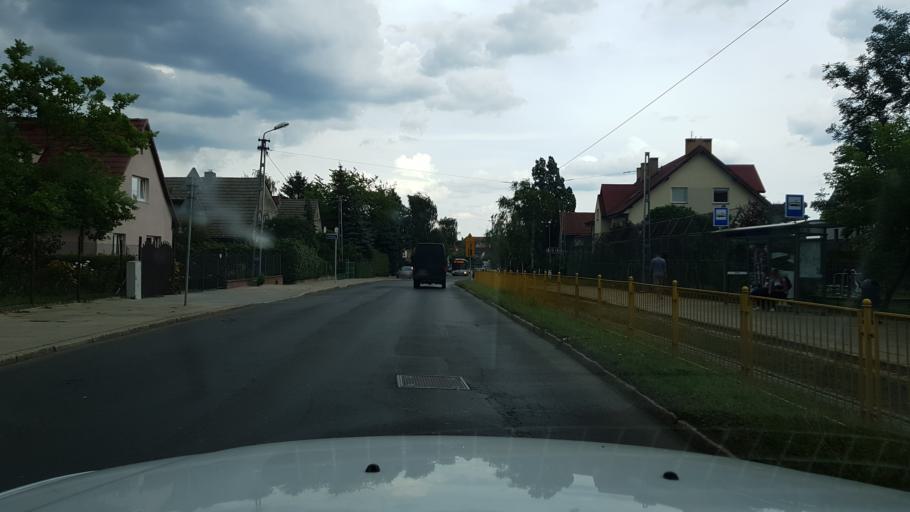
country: PL
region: West Pomeranian Voivodeship
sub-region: Powiat policki
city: Przeclaw
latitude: 53.4214
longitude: 14.4924
